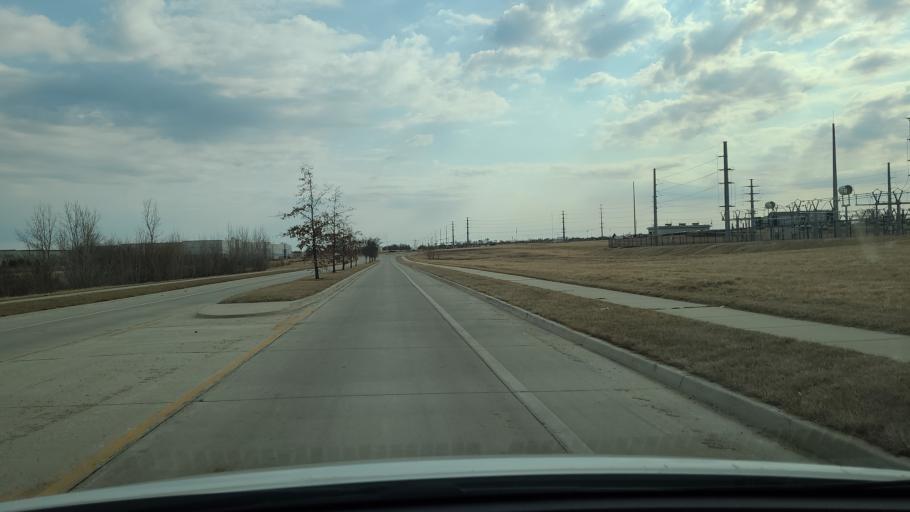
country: US
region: Kansas
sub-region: Douglas County
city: Lawrence
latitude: 38.9483
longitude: -95.2043
